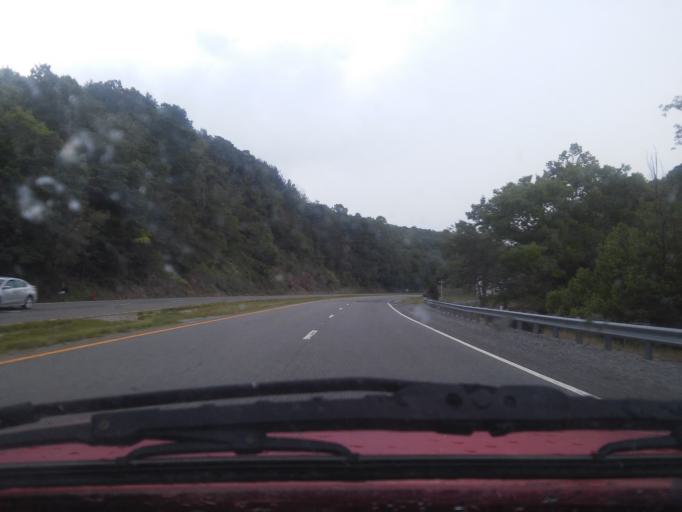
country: US
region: Virginia
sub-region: Montgomery County
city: Prices Fork
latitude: 37.3067
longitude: -80.5130
